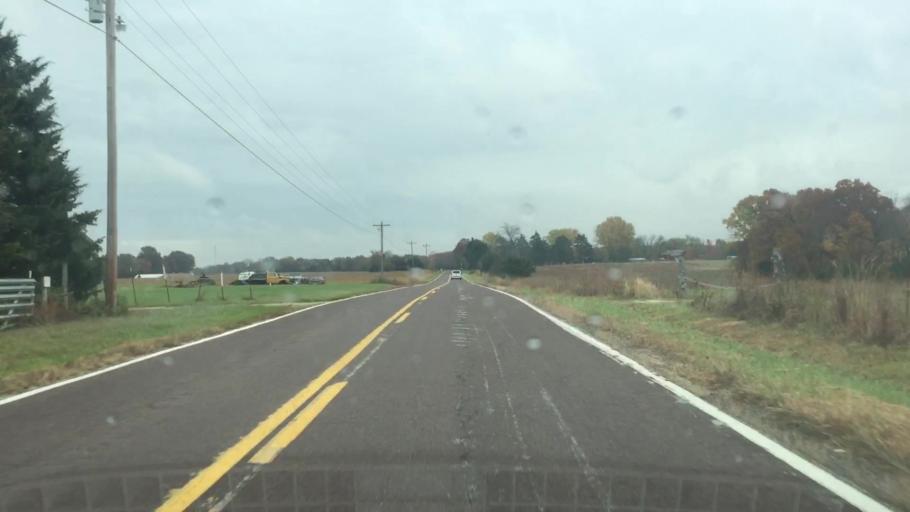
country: US
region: Missouri
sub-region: Callaway County
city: Fulton
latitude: 38.7826
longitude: -91.8228
